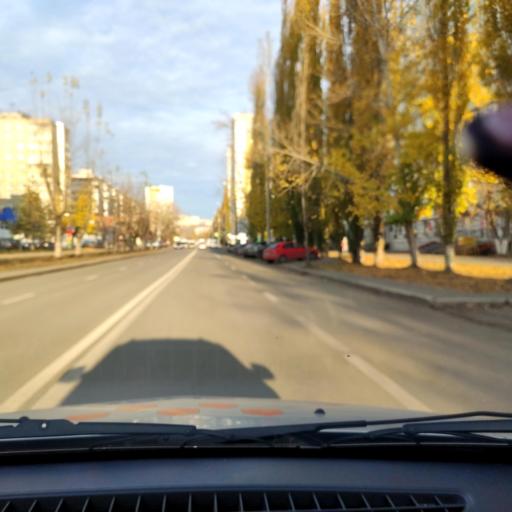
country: RU
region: Bashkortostan
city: Ufa
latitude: 54.7662
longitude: 56.0626
